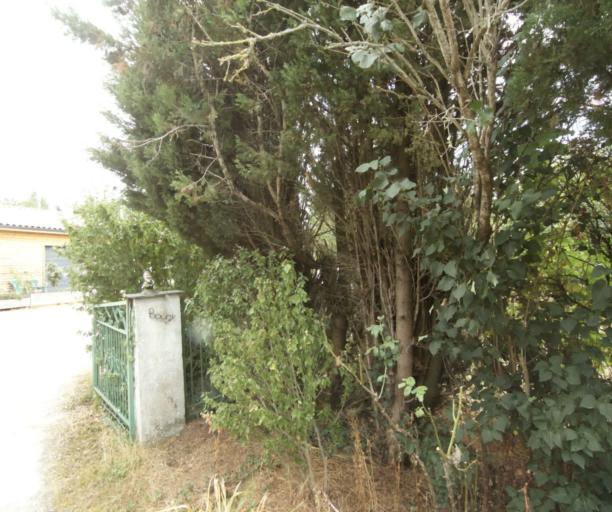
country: FR
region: Midi-Pyrenees
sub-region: Departement de la Haute-Garonne
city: Revel
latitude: 43.4527
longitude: 2.0296
